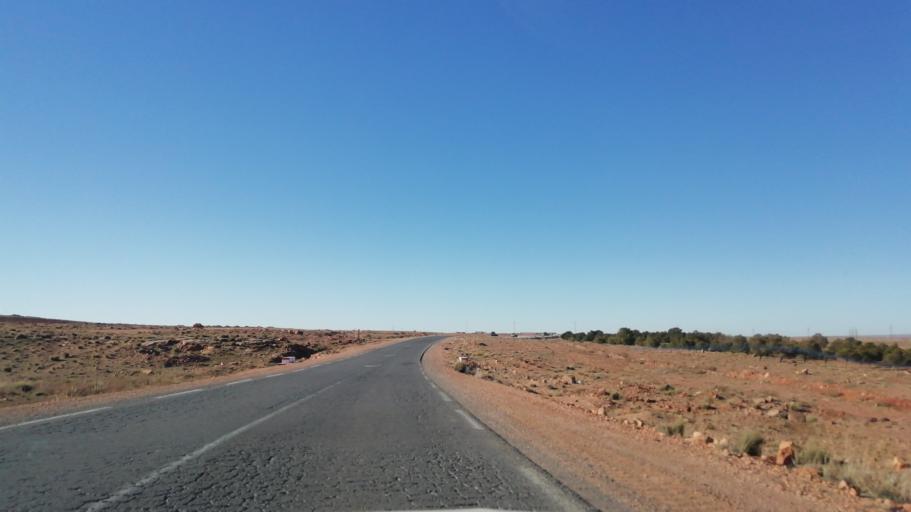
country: DZ
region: El Bayadh
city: El Bayadh
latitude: 33.6691
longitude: 0.9306
